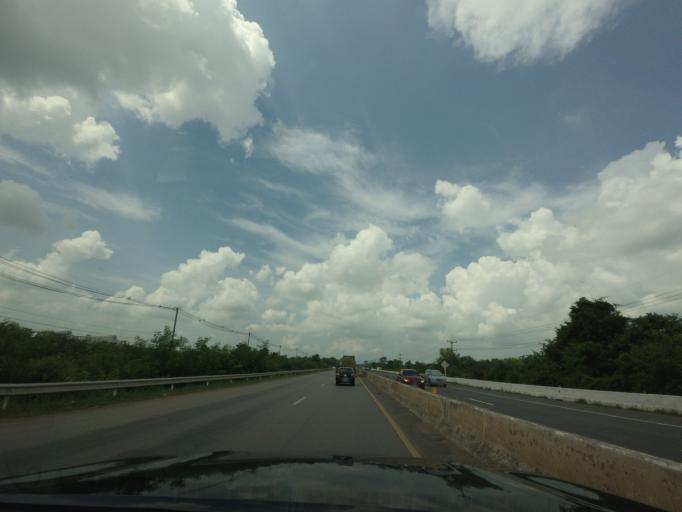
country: TH
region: Khon Kaen
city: Nong Ruea
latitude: 16.4916
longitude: 102.4257
